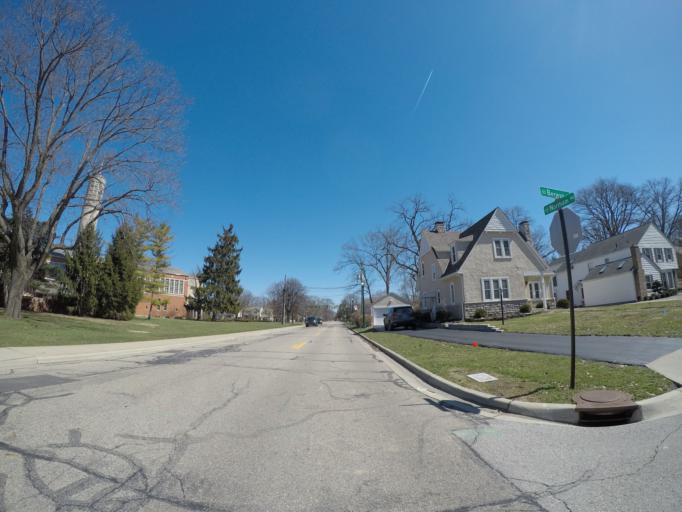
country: US
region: Ohio
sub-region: Franklin County
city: Upper Arlington
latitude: 40.0120
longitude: -83.0616
